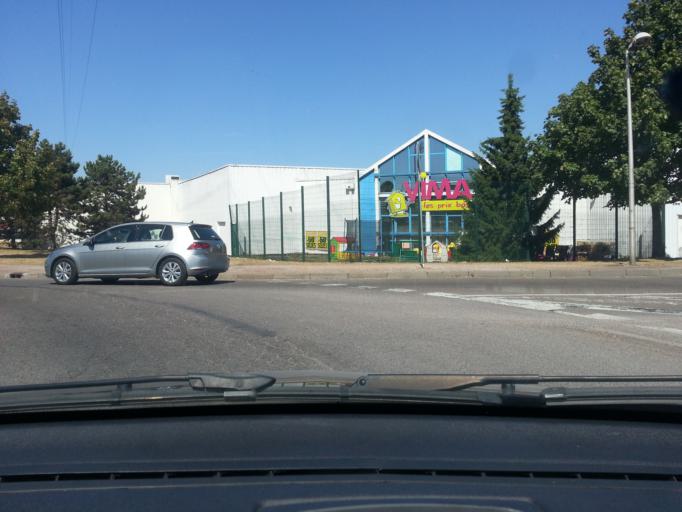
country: FR
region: Bourgogne
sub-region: Departement de la Cote-d'Or
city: Perrigny-les-Dijon
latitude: 47.2793
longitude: 5.0170
